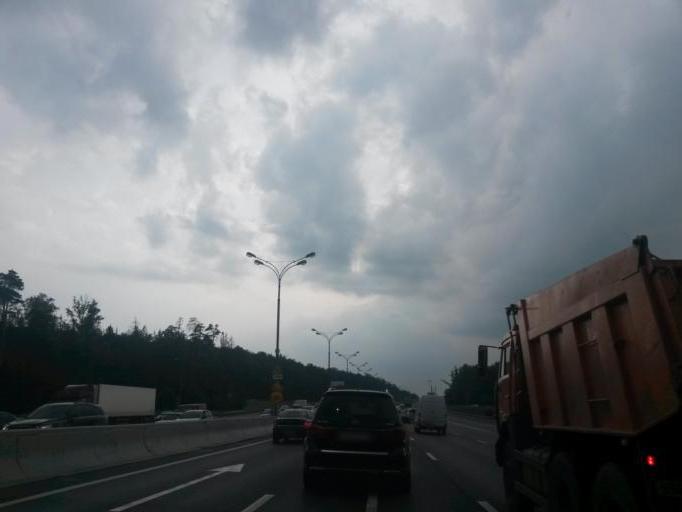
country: RU
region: Moscow
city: Biryulevo
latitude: 55.5758
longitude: 37.6875
